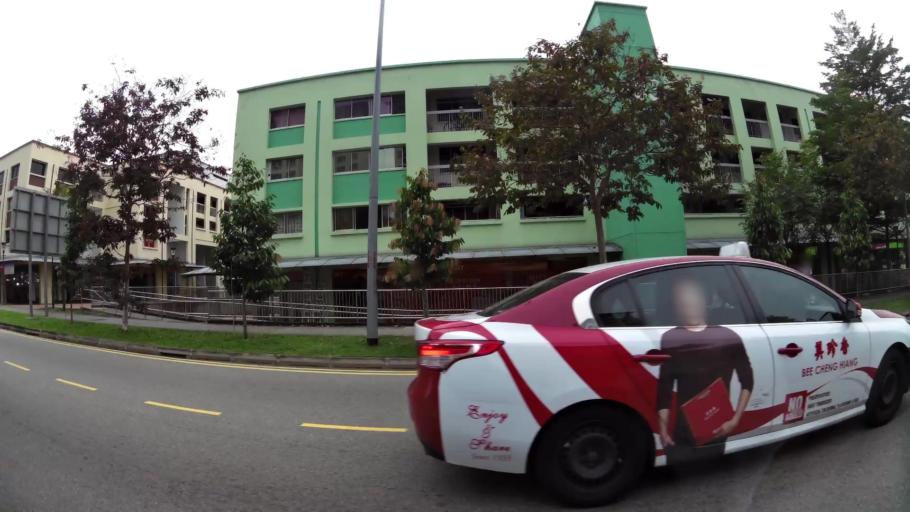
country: SG
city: Singapore
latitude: 1.3708
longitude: 103.8728
